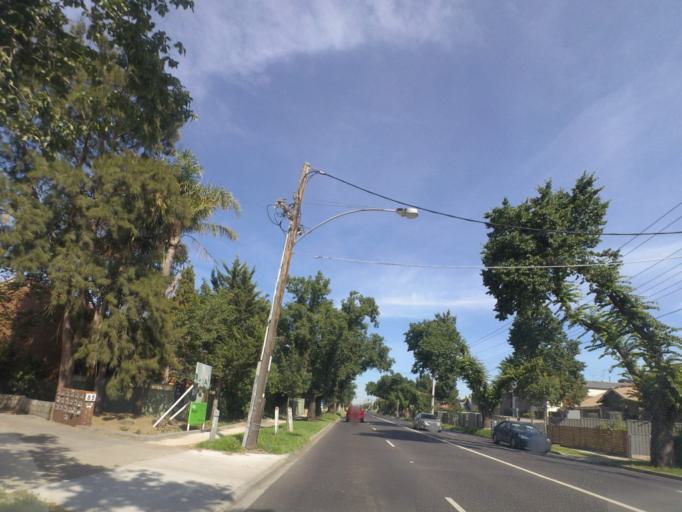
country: AU
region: Victoria
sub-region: Maribyrnong
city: Maribyrnong
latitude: -37.7867
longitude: 144.8783
